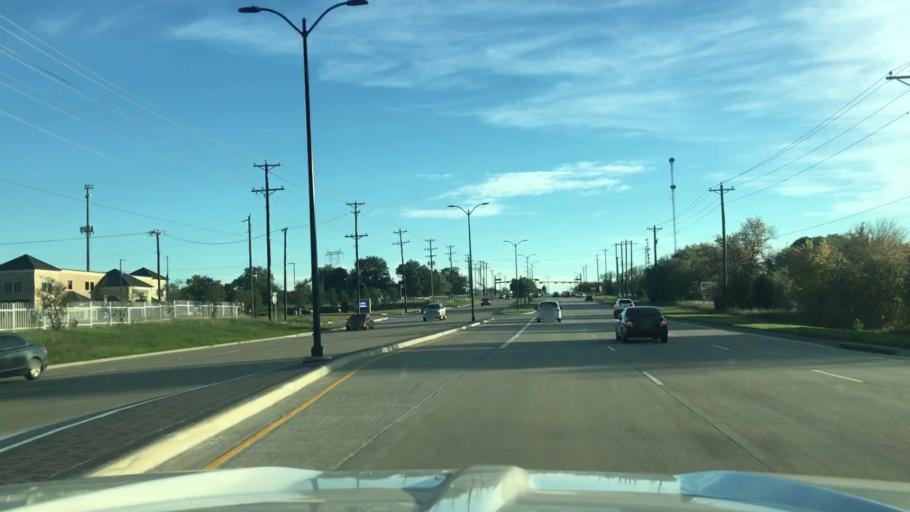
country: US
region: Texas
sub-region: Collin County
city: Prosper
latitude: 33.2077
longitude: -96.8028
